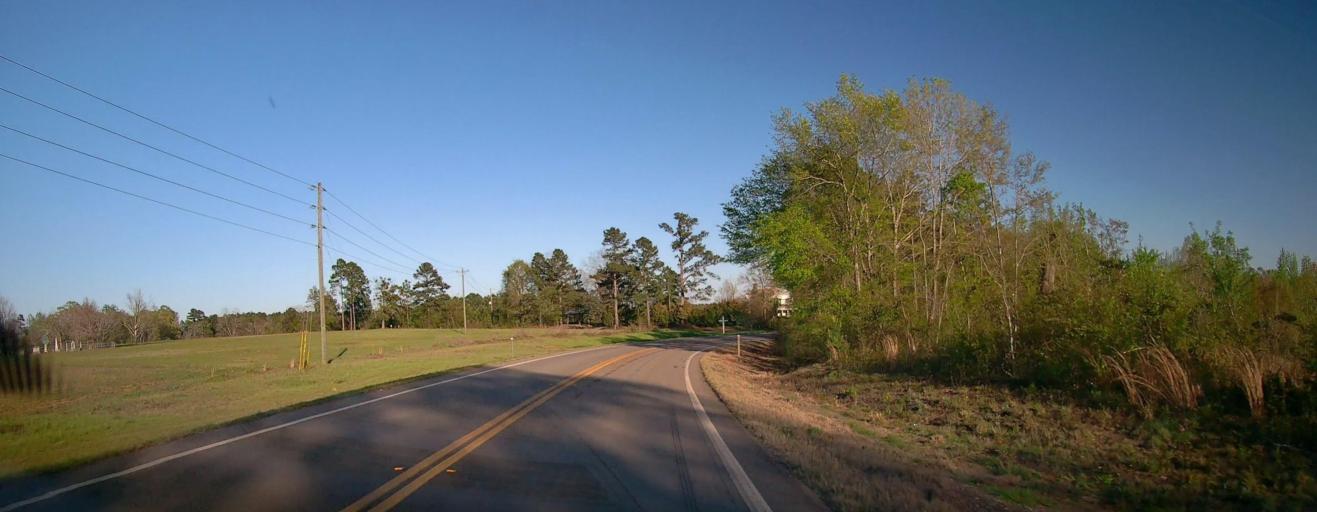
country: US
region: Georgia
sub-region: Wilkinson County
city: Irwinton
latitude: 32.8568
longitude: -83.0685
